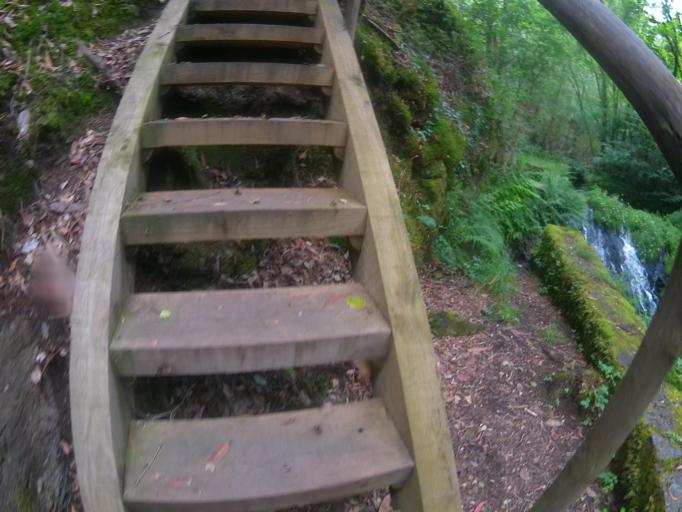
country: PT
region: Aveiro
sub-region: Albergaria-A-Velha
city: Branca
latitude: 40.7540
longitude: -8.4261
